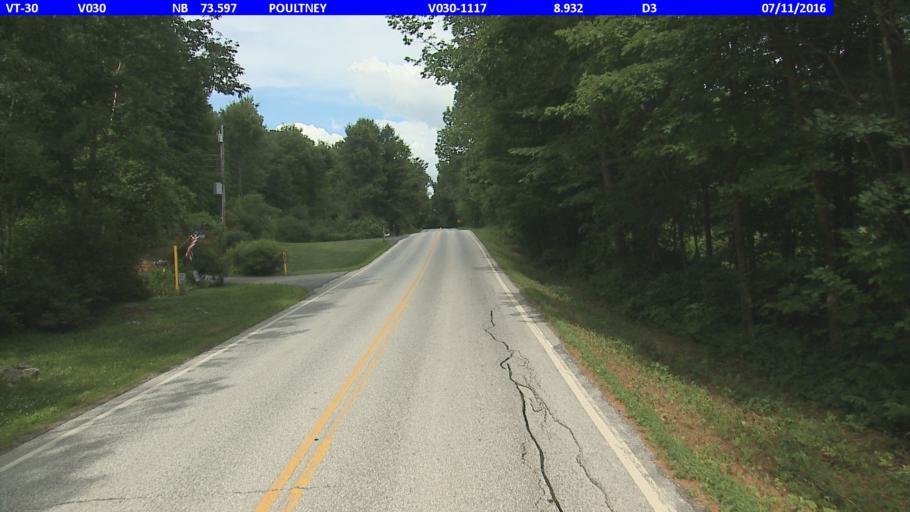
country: US
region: Vermont
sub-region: Rutland County
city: Castleton
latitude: 43.5781
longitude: -73.2165
